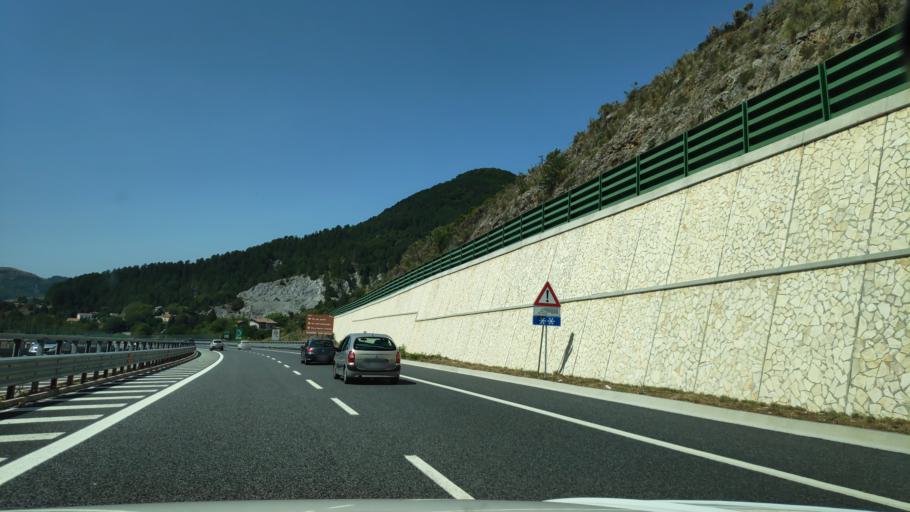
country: IT
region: Calabria
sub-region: Provincia di Cosenza
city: Mormanno
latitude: 39.8843
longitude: 16.0159
